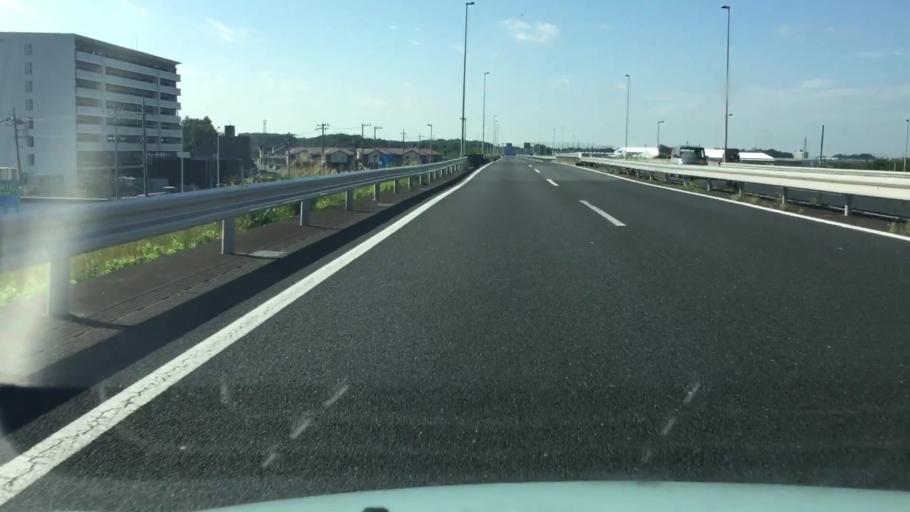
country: JP
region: Tochigi
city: Mooka
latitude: 36.4574
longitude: 139.9791
